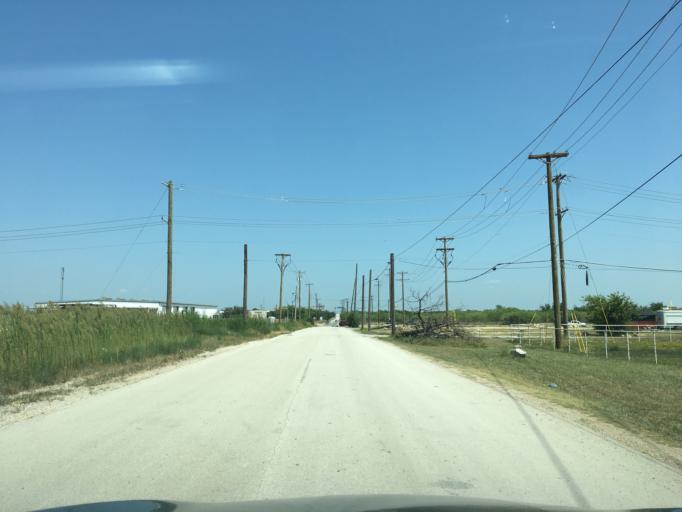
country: US
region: Texas
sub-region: Tarrant County
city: Crowley
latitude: 32.6143
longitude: -97.3529
